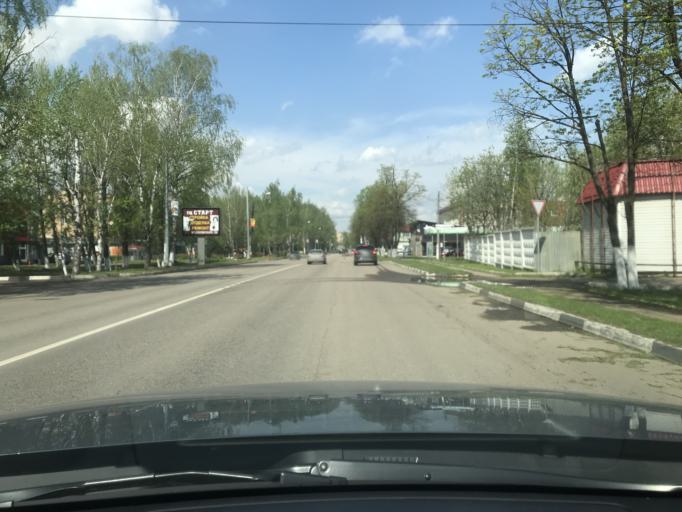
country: RU
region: Moskovskaya
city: Naro-Fominsk
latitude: 55.3787
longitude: 36.7596
